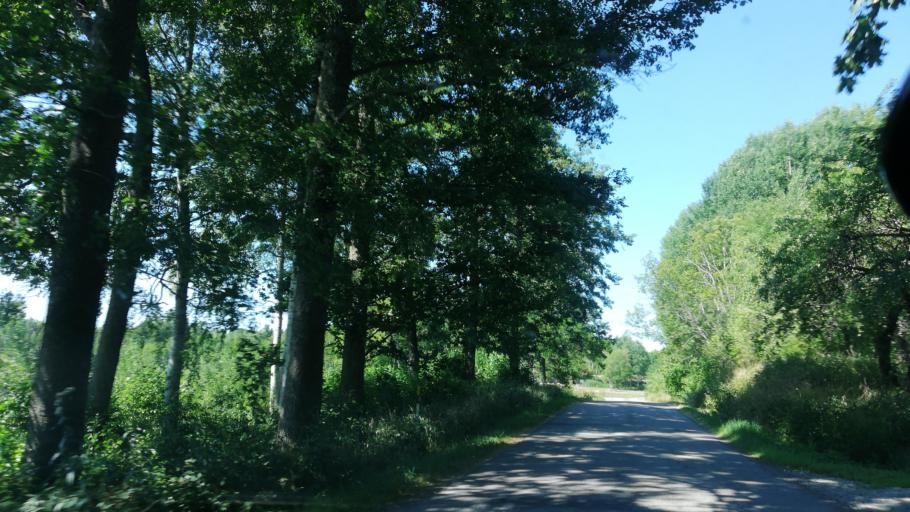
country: SE
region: OEstergoetland
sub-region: Finspangs Kommun
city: Finspang
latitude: 58.7331
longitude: 15.7190
